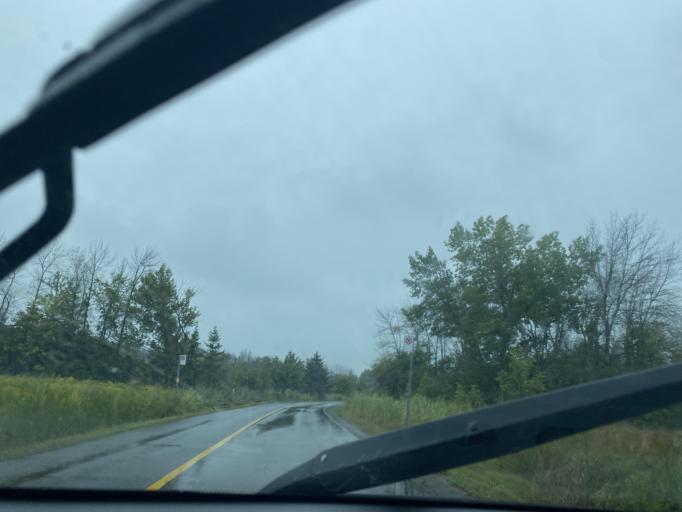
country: CA
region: Quebec
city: Baie-D'Urfe
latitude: 45.4639
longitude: -73.9223
